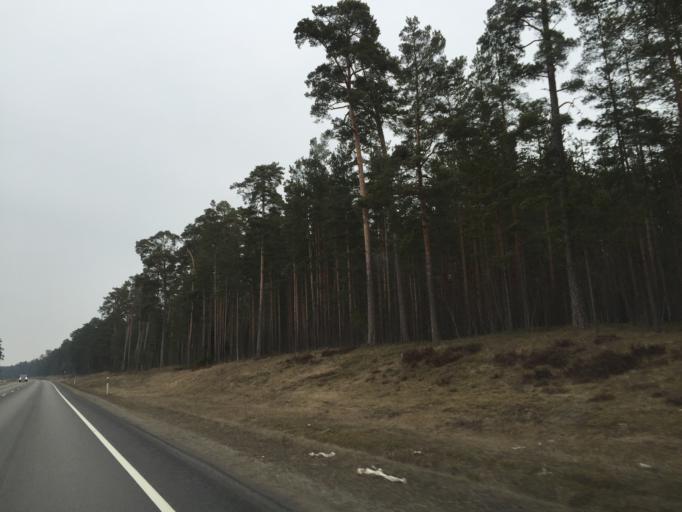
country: EE
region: Paernumaa
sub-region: Paernu linn
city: Parnu
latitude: 58.1822
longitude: 24.4927
